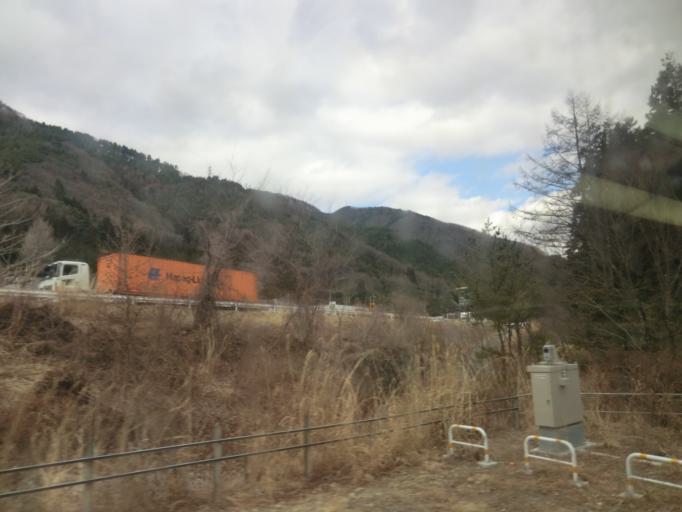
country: JP
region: Nagano
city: Shiojiri
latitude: 36.0233
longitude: 137.8698
